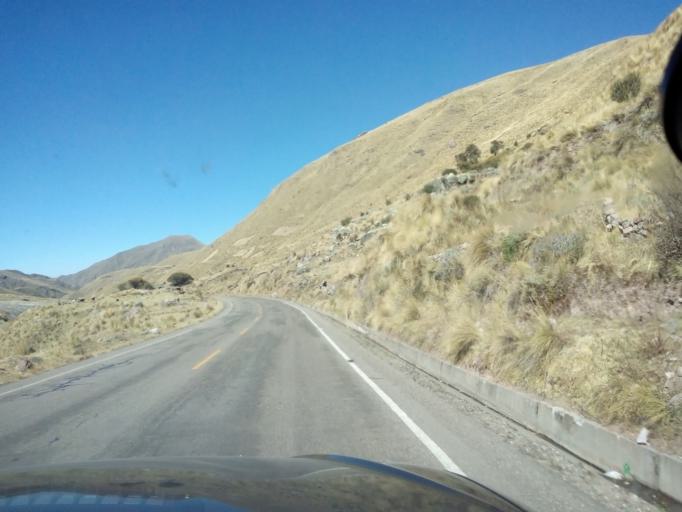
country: PE
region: Ayacucho
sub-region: Provincia de Cangallo
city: Totos
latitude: -13.3428
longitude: -74.5649
